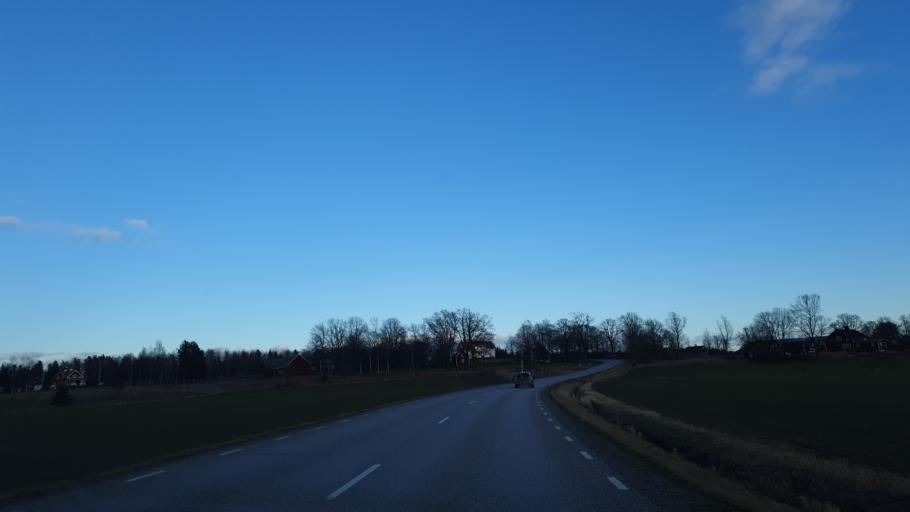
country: SE
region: OErebro
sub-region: Orebro Kommun
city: Garphyttan
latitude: 59.3401
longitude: 15.0581
